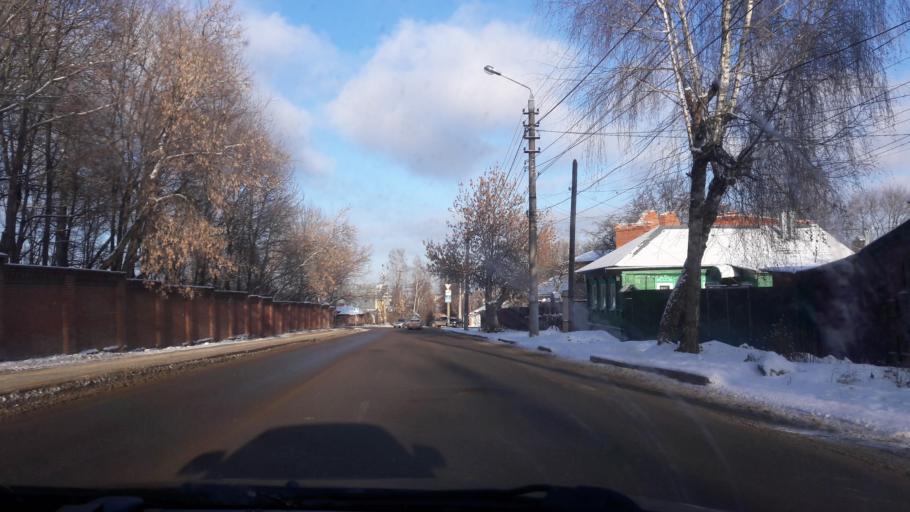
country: RU
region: Tula
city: Tula
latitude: 54.1792
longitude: 37.6160
